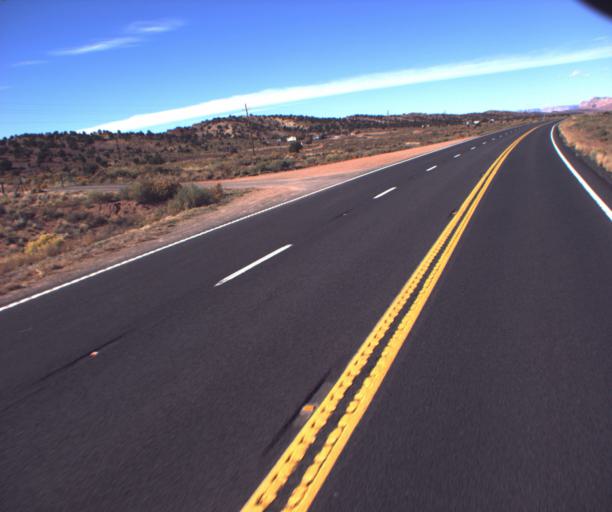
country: US
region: Arizona
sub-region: Coconino County
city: Tuba City
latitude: 36.4066
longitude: -111.5361
